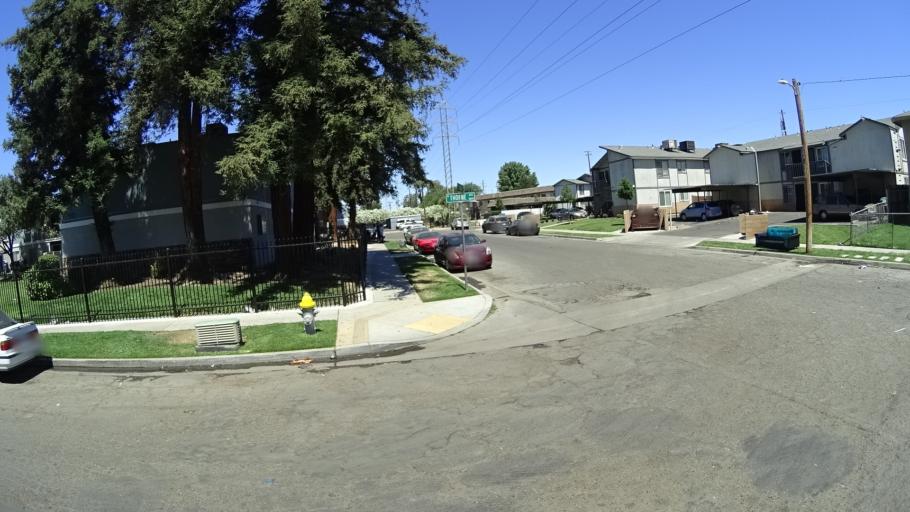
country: US
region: California
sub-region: Fresno County
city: Fresno
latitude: 36.7877
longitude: -119.8130
